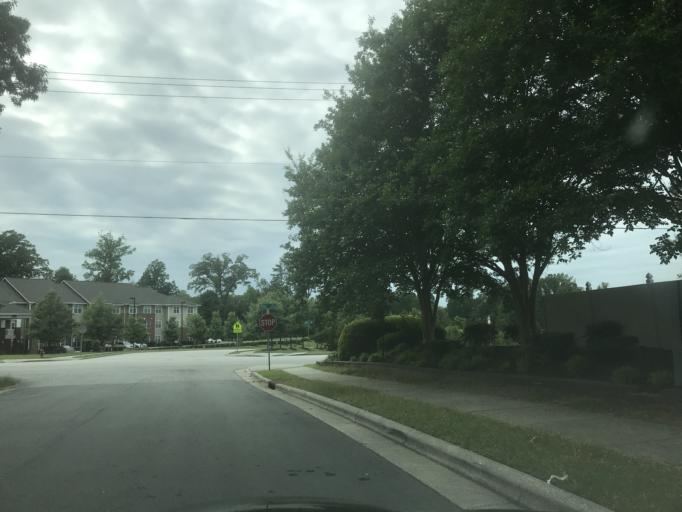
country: US
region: North Carolina
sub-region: Wake County
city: Knightdale
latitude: 35.8686
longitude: -78.5598
